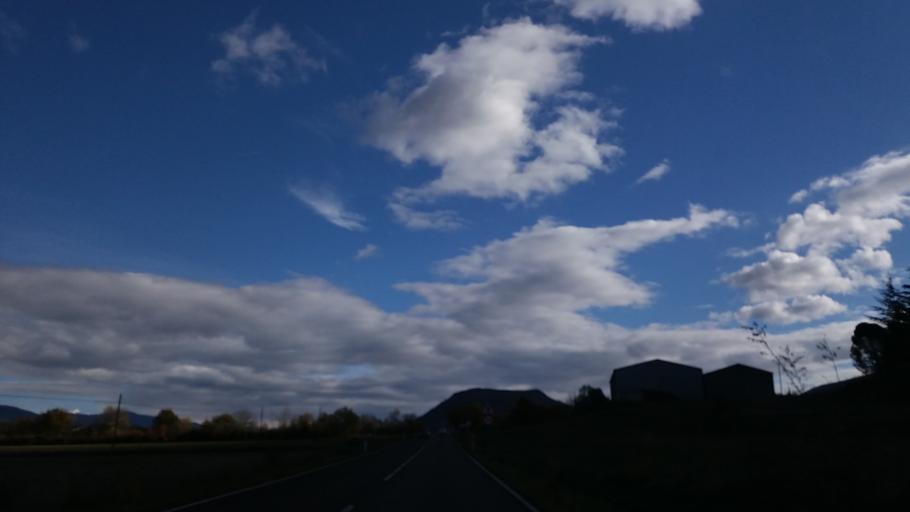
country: ES
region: Aragon
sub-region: Provincia de Huesca
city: Santa Cruz de la Seros
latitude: 42.5572
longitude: -0.7065
